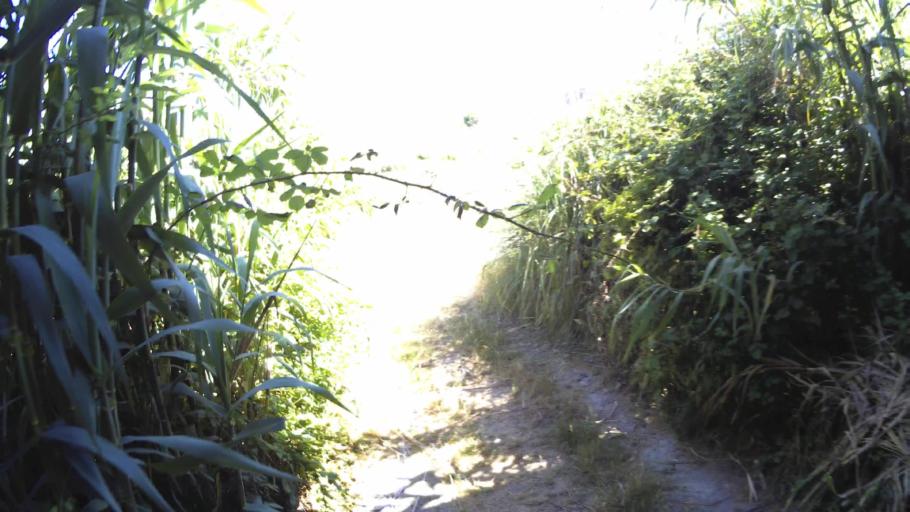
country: PT
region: Aveiro
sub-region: Aveiro
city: Aveiro
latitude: 40.6541
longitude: -8.6409
